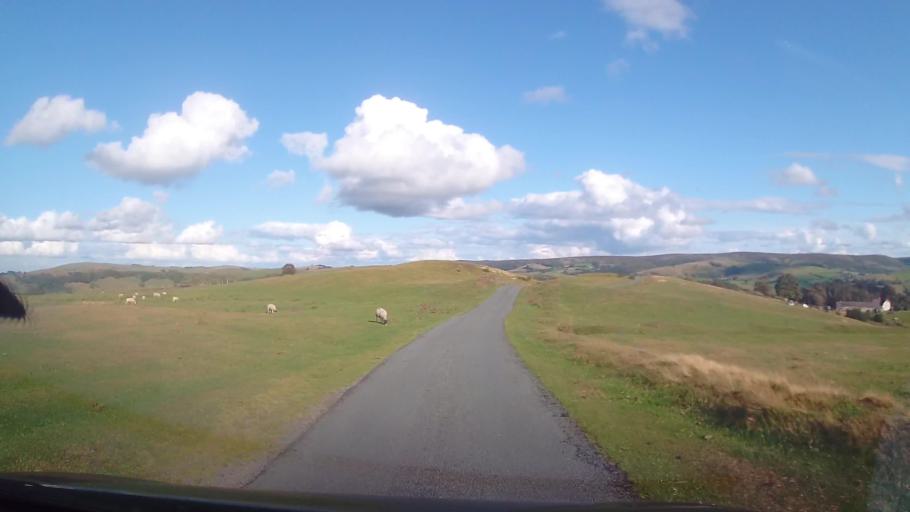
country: GB
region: England
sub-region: Shropshire
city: Norbury
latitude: 52.5730
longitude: -2.9236
